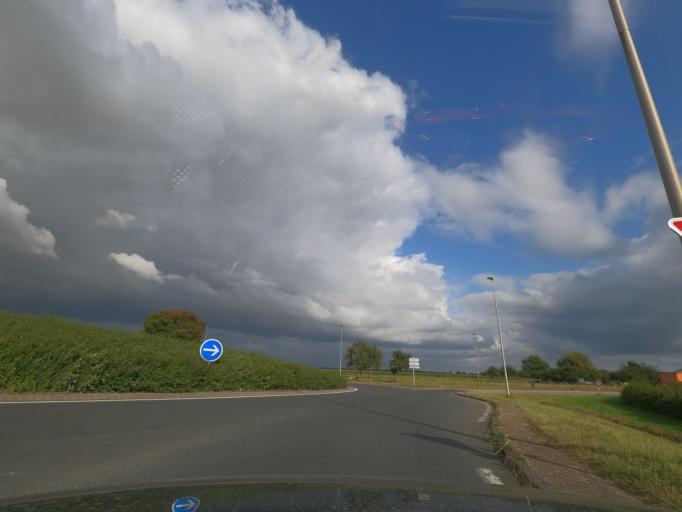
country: FR
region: Haute-Normandie
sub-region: Departement de l'Eure
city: Bernay
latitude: 49.1083
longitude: 0.5897
